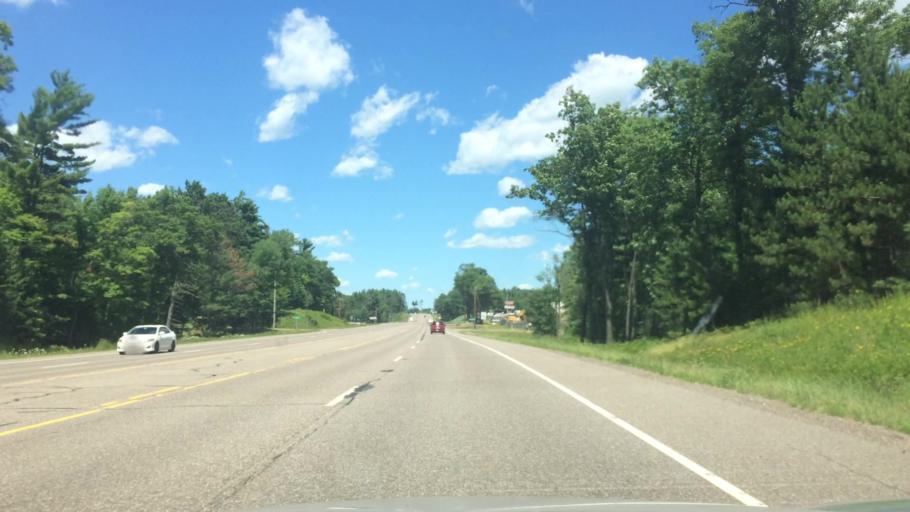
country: US
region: Wisconsin
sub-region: Vilas County
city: Lac du Flambeau
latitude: 45.8406
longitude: -89.7074
